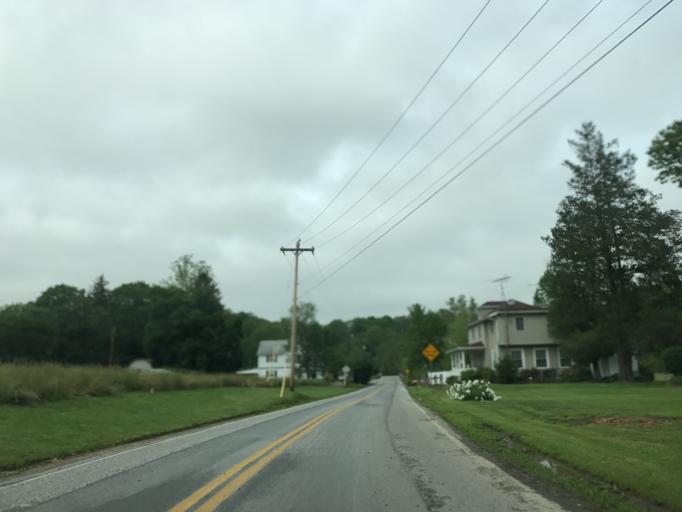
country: US
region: Pennsylvania
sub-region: York County
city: Susquehanna Trails
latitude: 39.7841
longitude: -76.4077
